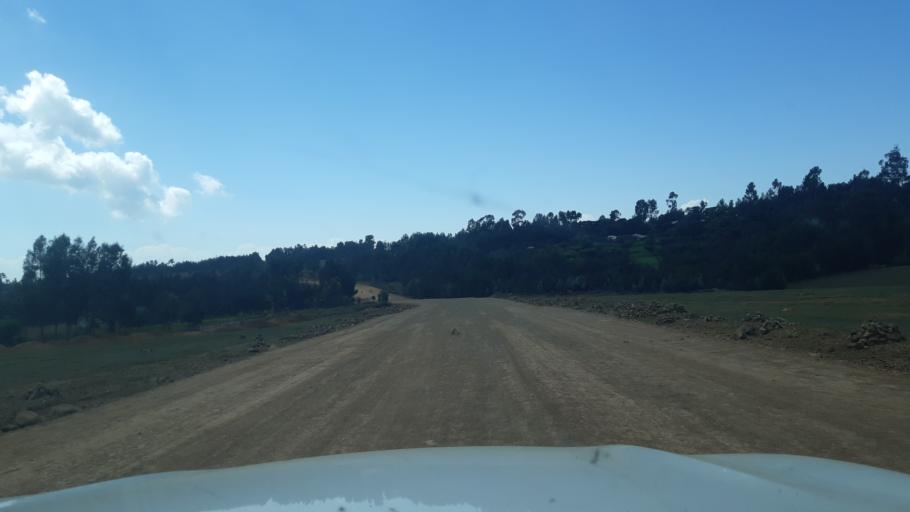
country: ET
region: Amhara
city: Dabat
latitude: 13.3681
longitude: 37.3838
